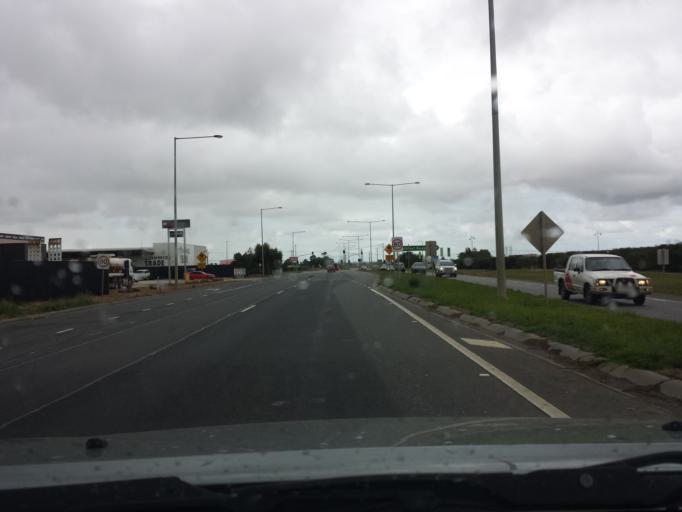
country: AU
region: Victoria
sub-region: Cardinia
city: Pakenham South
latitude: -38.0960
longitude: 145.4894
